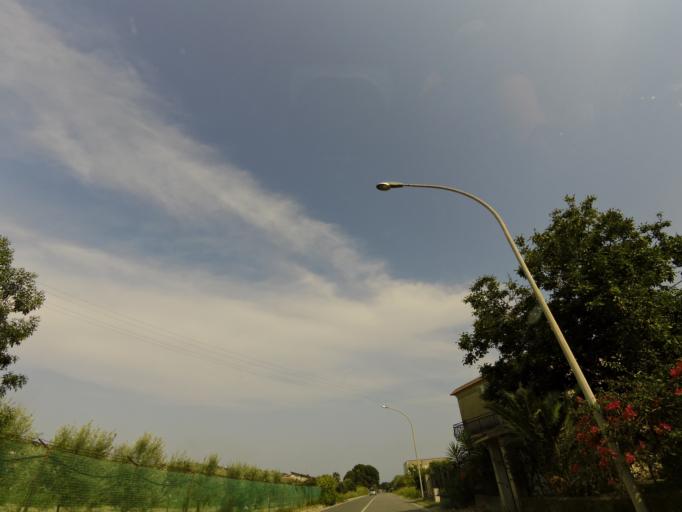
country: IT
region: Calabria
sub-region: Provincia di Reggio Calabria
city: Monasterace
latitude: 38.4384
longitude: 16.5519
